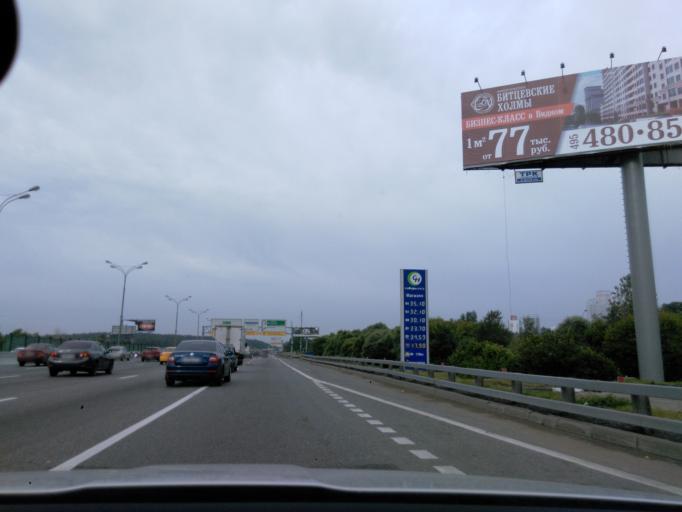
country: RU
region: Moscow
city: Biryulevo
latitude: 55.5794
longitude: 37.6969
